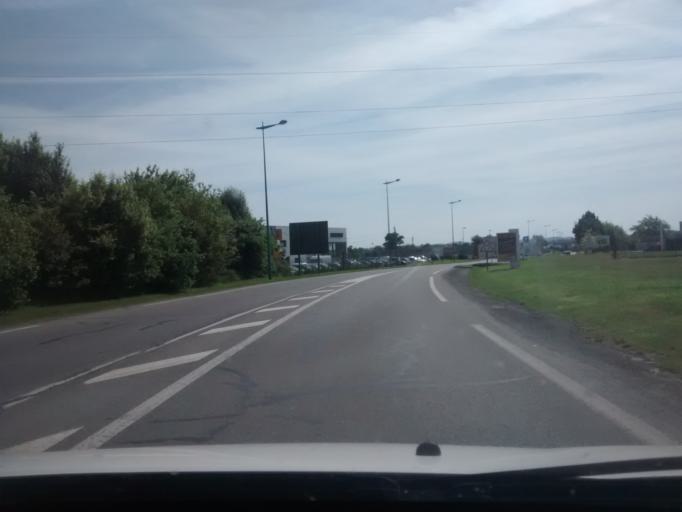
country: FR
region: Brittany
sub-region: Departement d'Ille-et-Vilaine
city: Saint-Brice-en-Cogles
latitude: 48.4166
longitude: -1.3870
